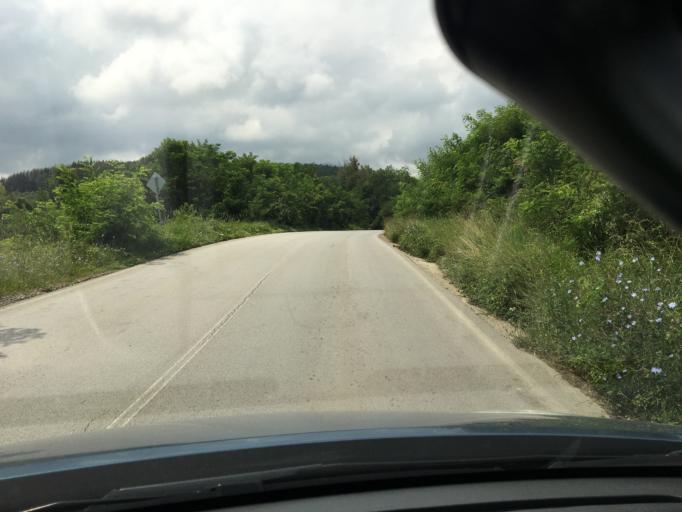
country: BG
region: Sofia-Capital
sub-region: Stolichna Obshtina
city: Sofia
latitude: 42.5981
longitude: 23.3681
